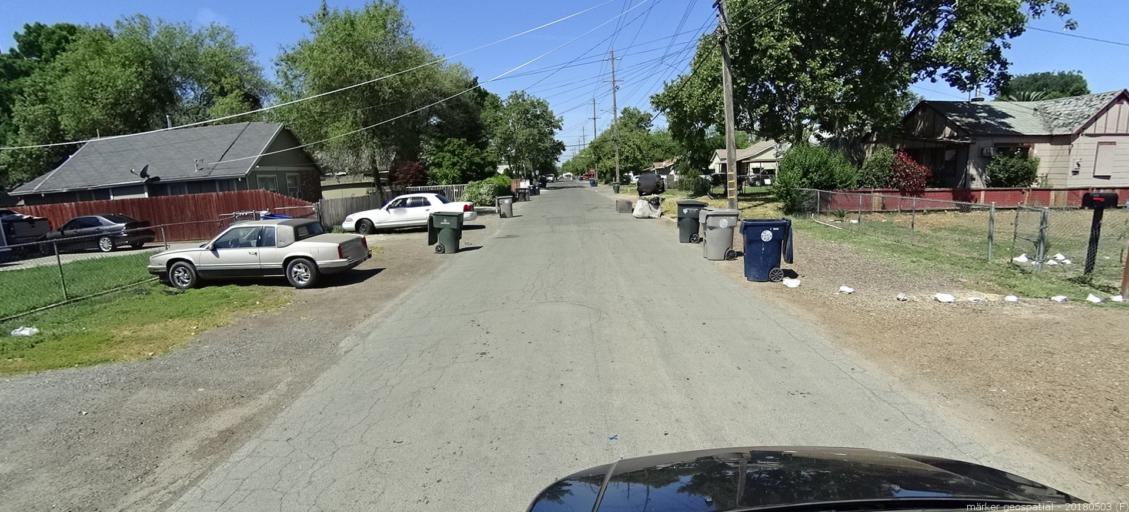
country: US
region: California
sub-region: Sacramento County
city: Arden-Arcade
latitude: 38.6129
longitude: -121.4402
